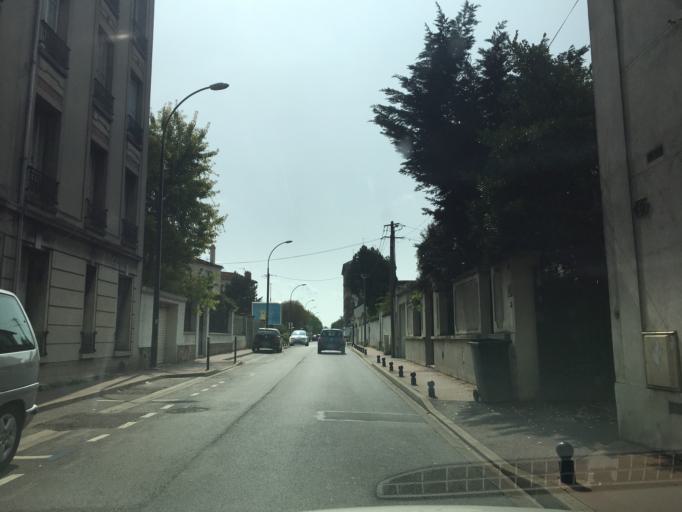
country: FR
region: Ile-de-France
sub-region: Departement du Val-de-Marne
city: Saint-Maur-des-Fosses
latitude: 48.8047
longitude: 2.4776
